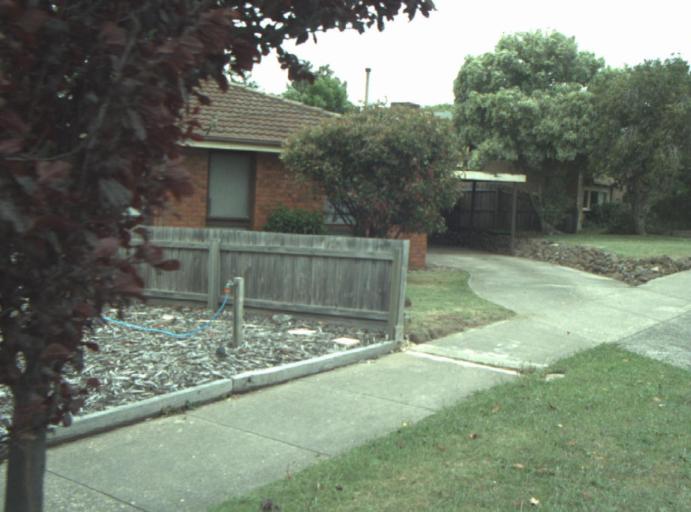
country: AU
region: Victoria
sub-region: Greater Geelong
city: Leopold
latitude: -38.1837
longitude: 144.4709
